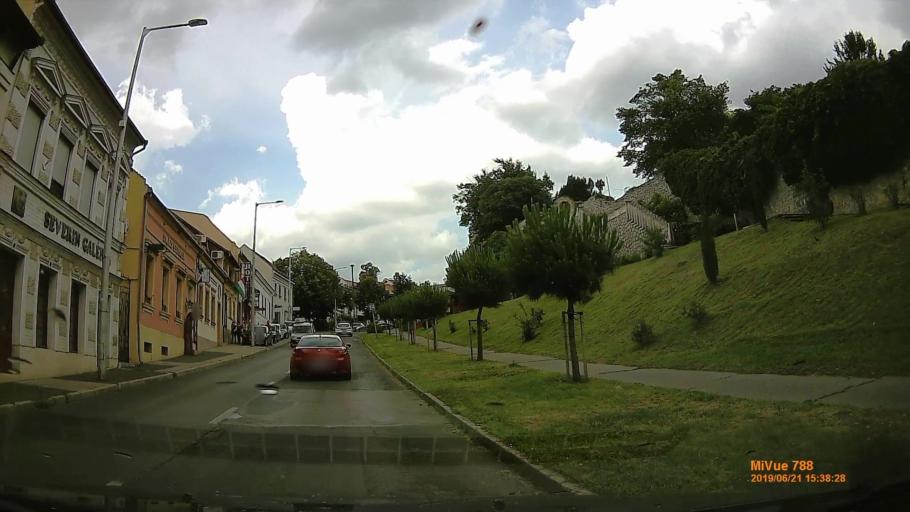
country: HU
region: Baranya
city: Pecs
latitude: 46.0761
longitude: 18.2210
